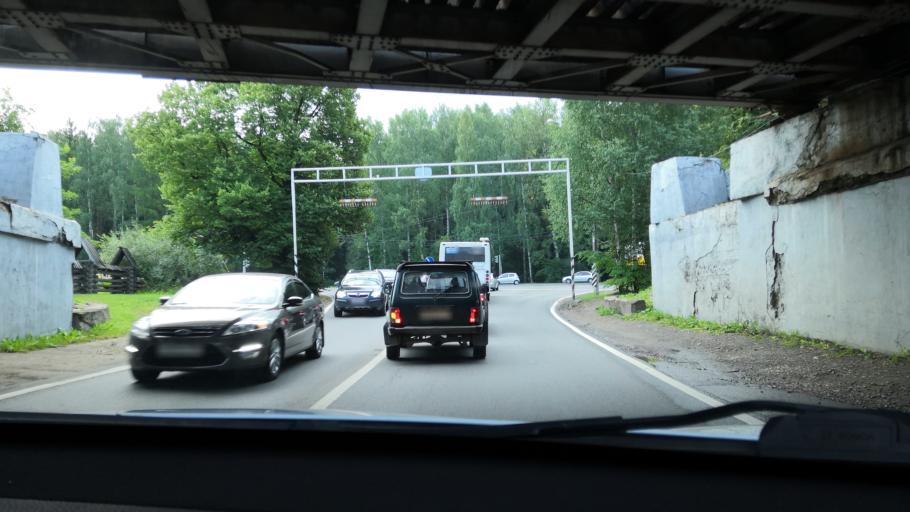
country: RU
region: St.-Petersburg
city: Pavlovsk
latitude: 59.6960
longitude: 30.4369
